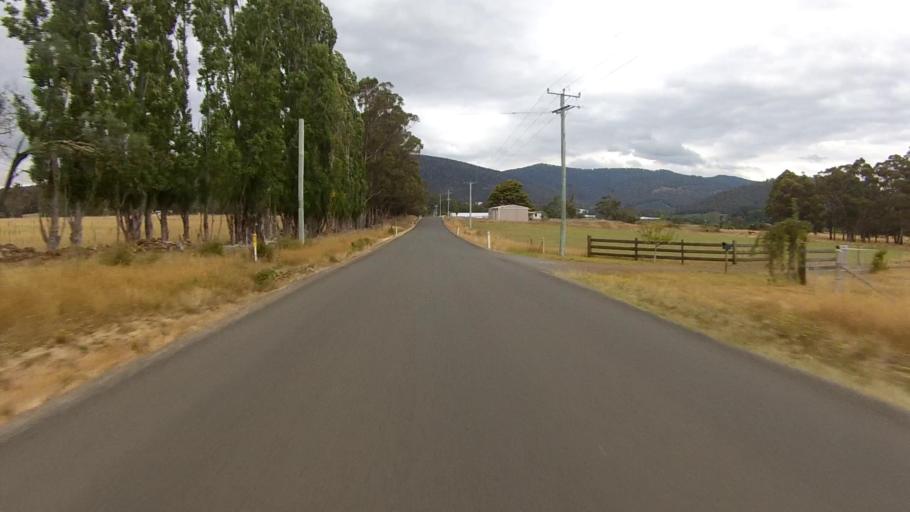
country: AU
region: Tasmania
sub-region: Huon Valley
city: Huonville
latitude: -42.9751
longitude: 147.0933
